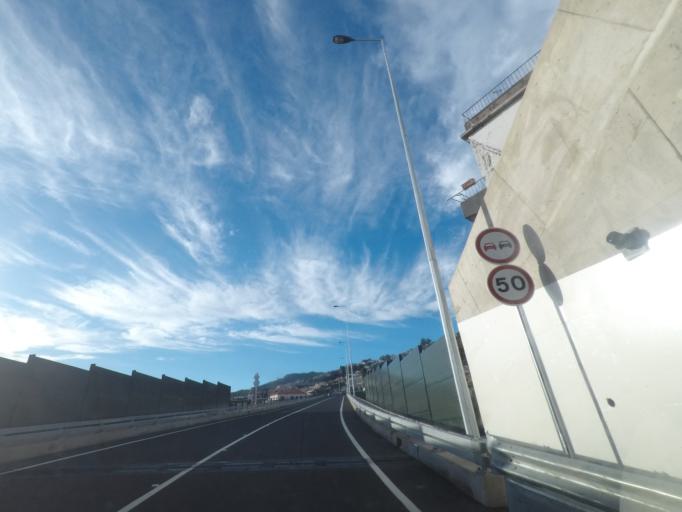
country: PT
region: Madeira
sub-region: Funchal
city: Nossa Senhora do Monte
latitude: 32.6763
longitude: -16.9386
